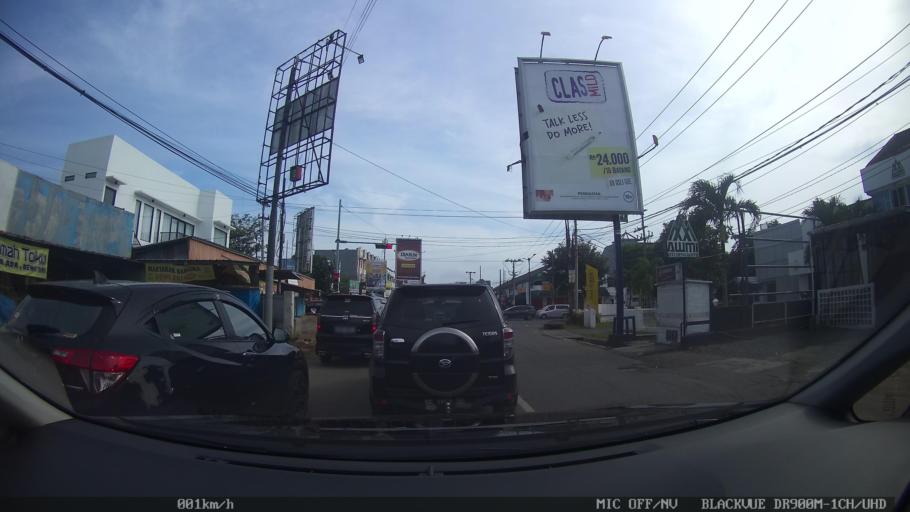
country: ID
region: Lampung
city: Kedaton
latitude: -5.3812
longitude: 105.2719
